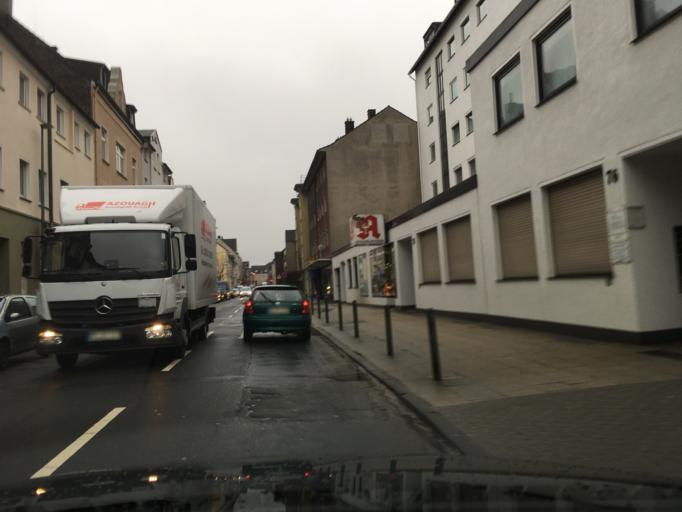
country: DE
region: North Rhine-Westphalia
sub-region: Regierungsbezirk Dusseldorf
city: Velbert
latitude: 51.3377
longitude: 7.0507
